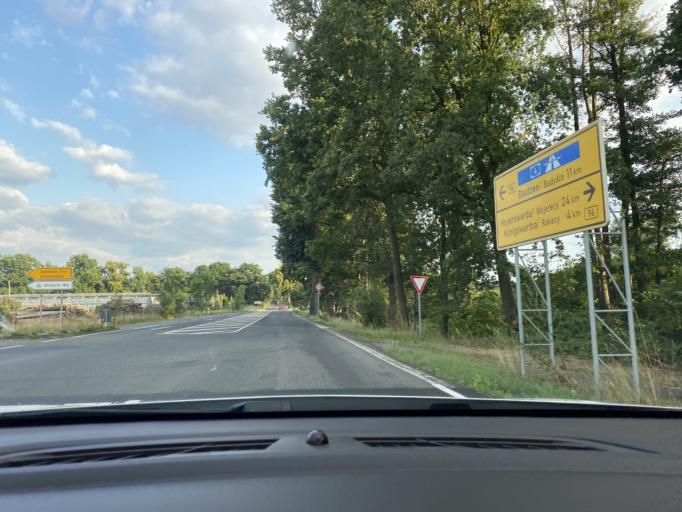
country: DE
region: Saxony
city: Neschwitz
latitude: 51.2717
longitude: 14.3426
